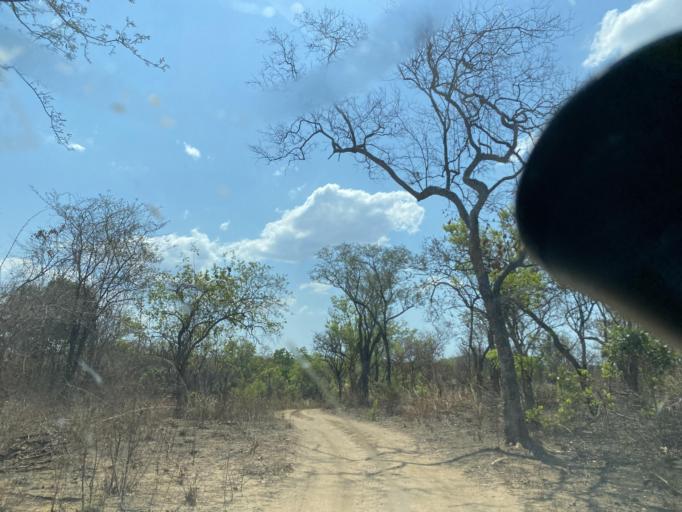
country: ZM
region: Lusaka
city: Chongwe
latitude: -15.0869
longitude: 29.4892
